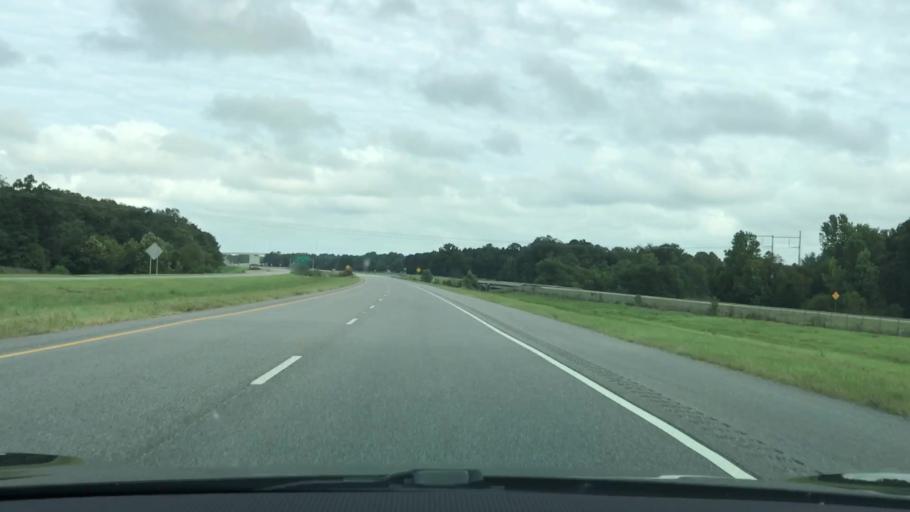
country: US
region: Alabama
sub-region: Montgomery County
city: Pike Road
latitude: 32.3530
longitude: -86.0674
